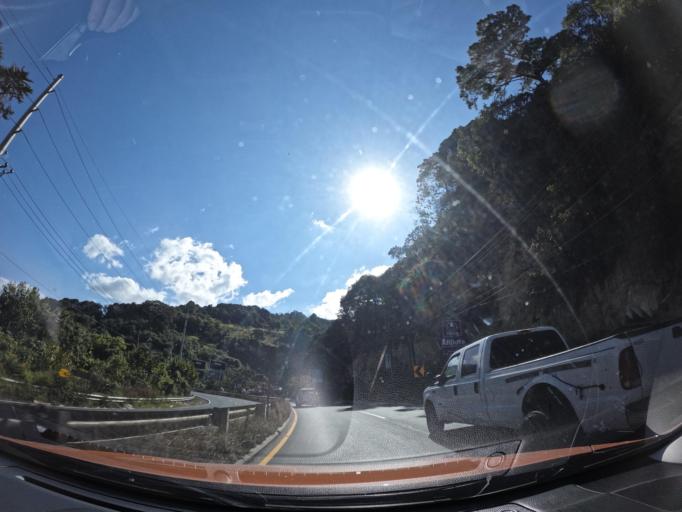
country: GT
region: Sacatepequez
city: San Bartolome Milpas Altas
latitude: 14.6203
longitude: -90.6845
